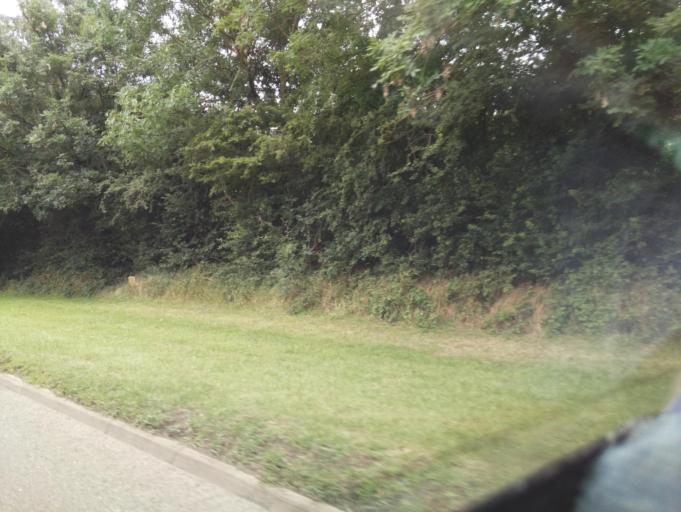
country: GB
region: England
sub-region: Northamptonshire
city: Corby
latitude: 52.5087
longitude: -0.7125
